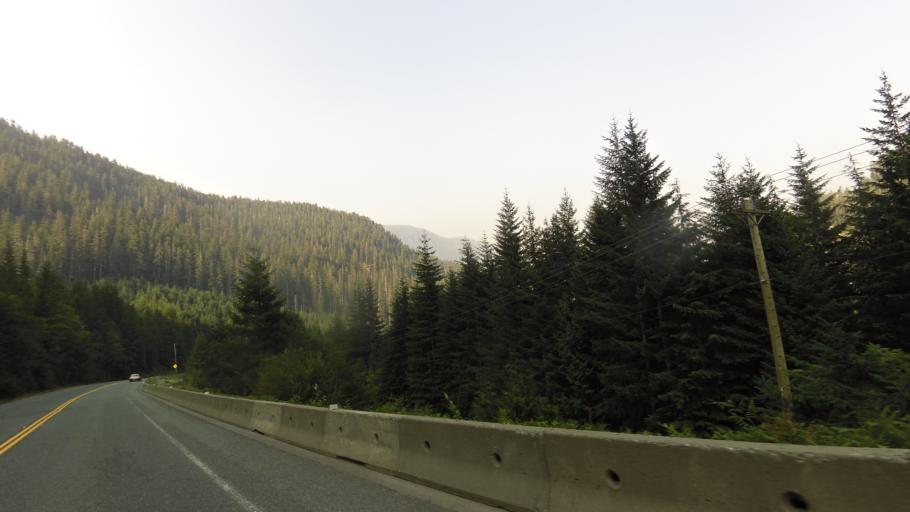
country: CA
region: British Columbia
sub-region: Regional District of Alberni-Clayoquot
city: Ucluelet
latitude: 49.2872
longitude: -125.3454
